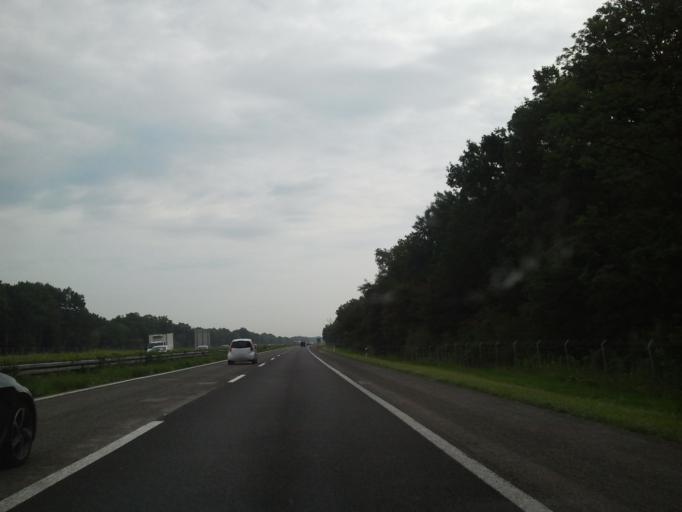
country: HR
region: Zagrebacka
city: Jastrebarsko
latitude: 45.6518
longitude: 15.6905
